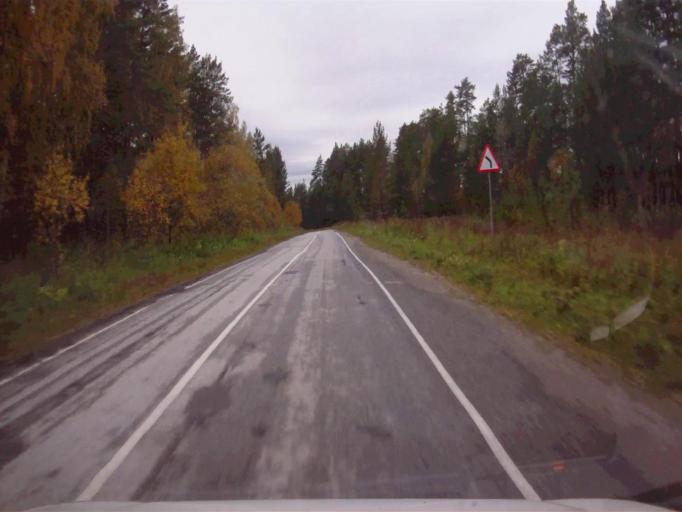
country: RU
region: Chelyabinsk
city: Nyazepetrovsk
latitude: 56.0561
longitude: 59.4725
